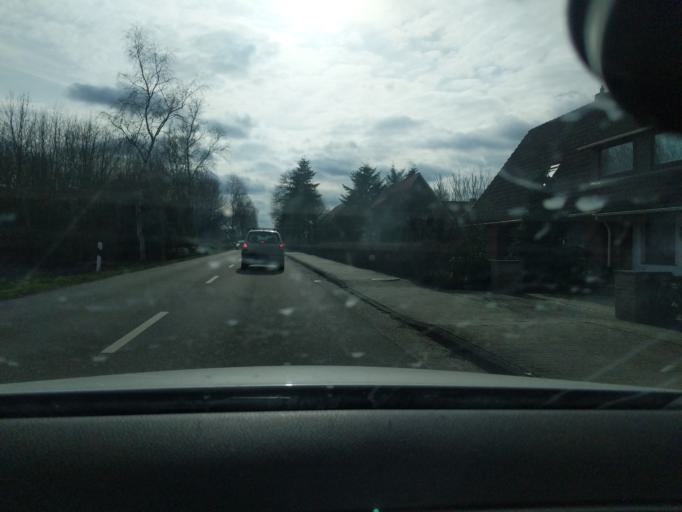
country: DE
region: Lower Saxony
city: Himmelpforten
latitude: 53.6277
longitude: 9.3193
